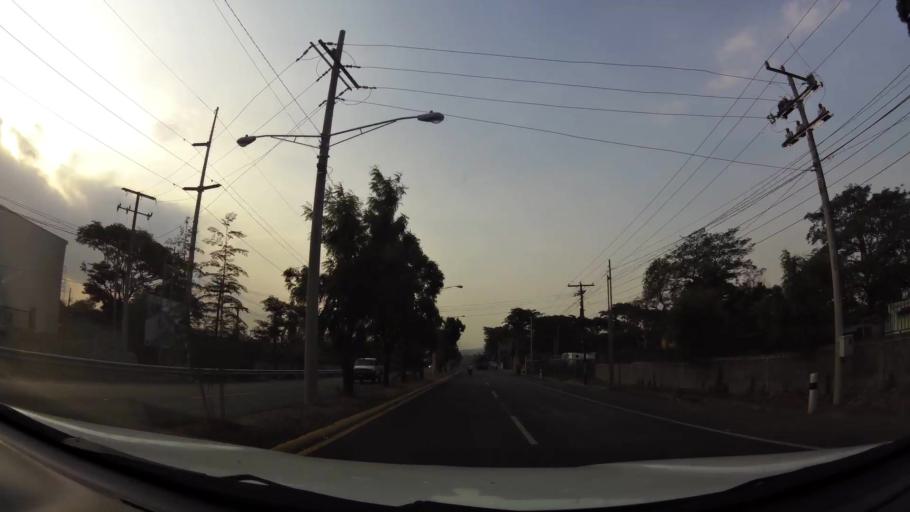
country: NI
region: Managua
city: Ciudad Sandino
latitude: 12.1482
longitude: -86.3360
